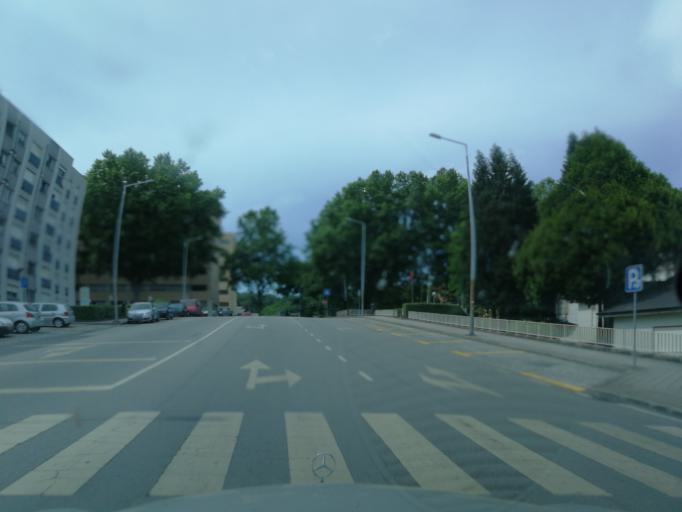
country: PT
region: Braga
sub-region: Vila Nova de Famalicao
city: Calendario
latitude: 41.4052
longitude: -8.5273
